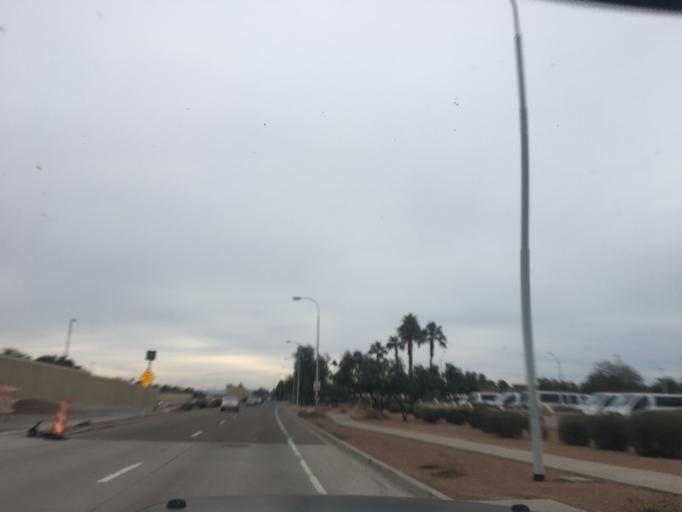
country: US
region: Arizona
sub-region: Maricopa County
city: San Carlos
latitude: 33.3217
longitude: -111.8934
